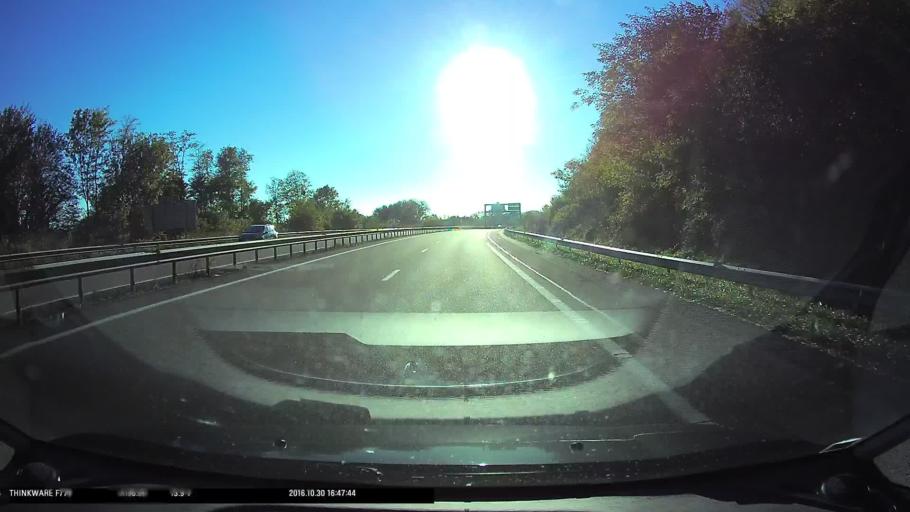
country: FR
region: Franche-Comte
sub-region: Departement du Doubs
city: Chatillon-le-Duc
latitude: 47.2826
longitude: 5.9996
